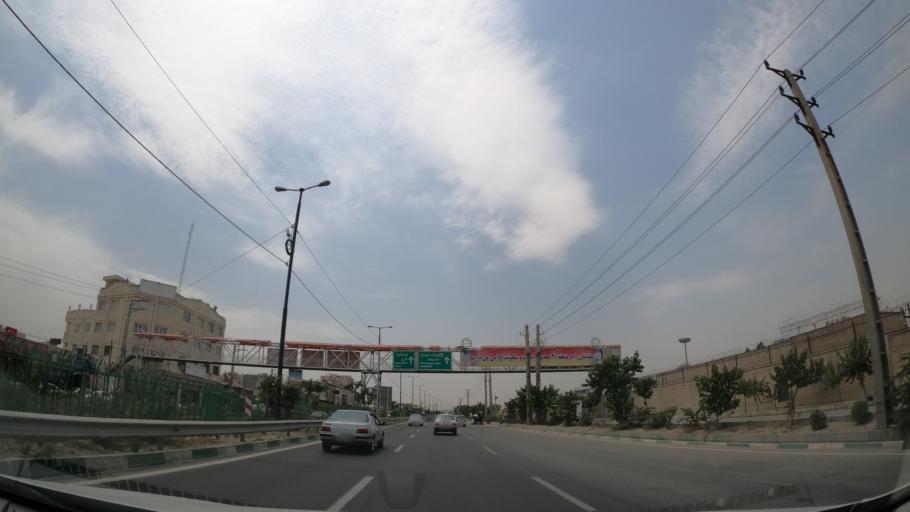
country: IR
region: Tehran
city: Eslamshahr
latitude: 35.6769
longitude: 51.2761
